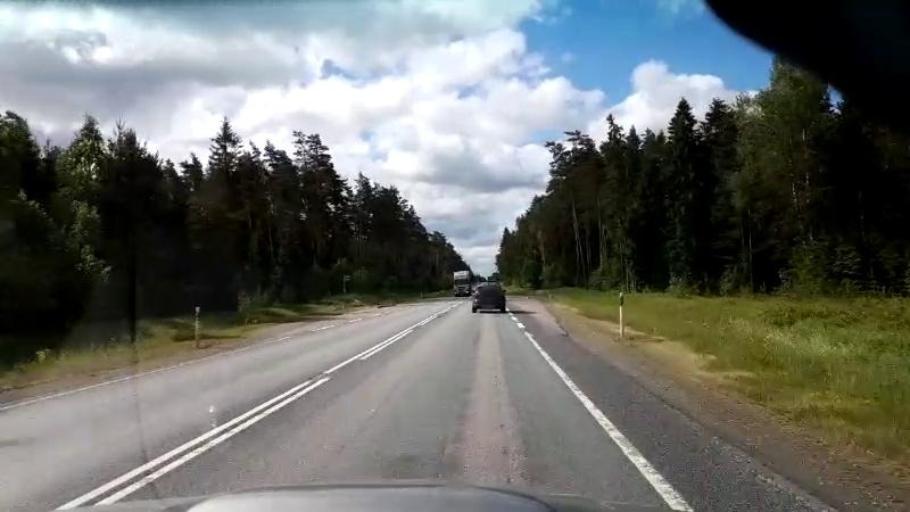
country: EE
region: Harju
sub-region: Saue linn
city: Saue
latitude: 59.2014
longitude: 24.4979
